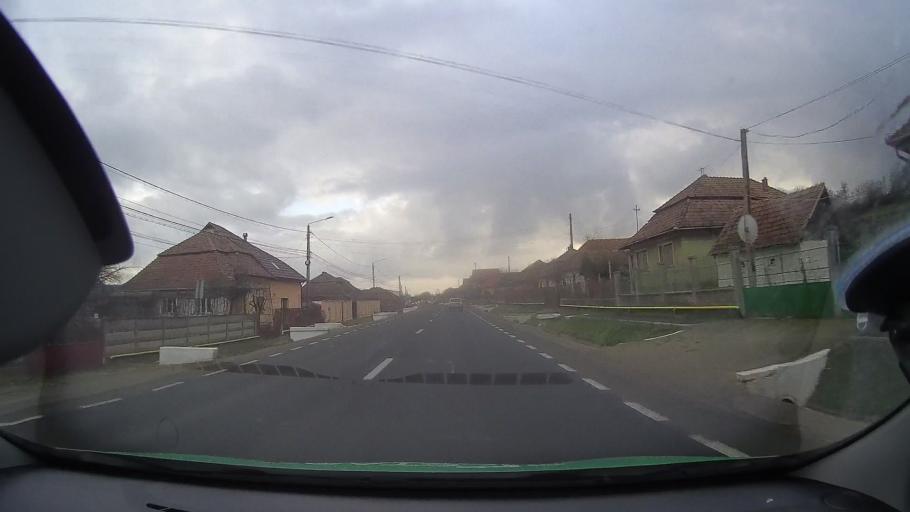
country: RO
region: Cluj
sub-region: Comuna Viisoara
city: Viisoara
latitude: 46.5142
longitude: 23.9172
